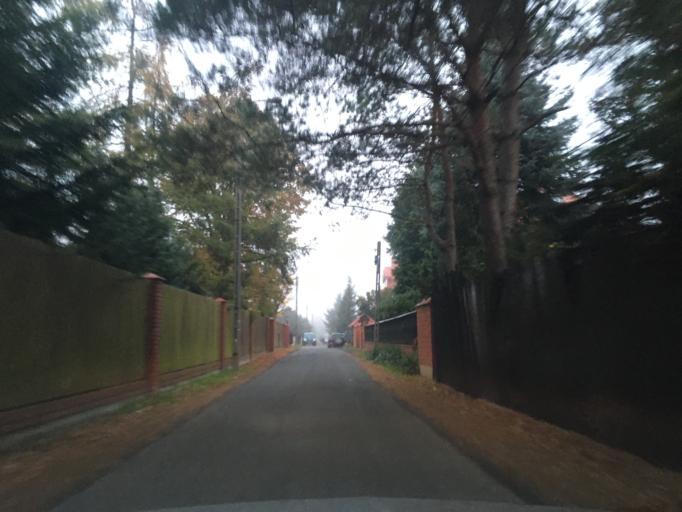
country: PL
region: Masovian Voivodeship
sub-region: Powiat pruszkowski
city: Brwinow
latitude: 52.1408
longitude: 20.7233
